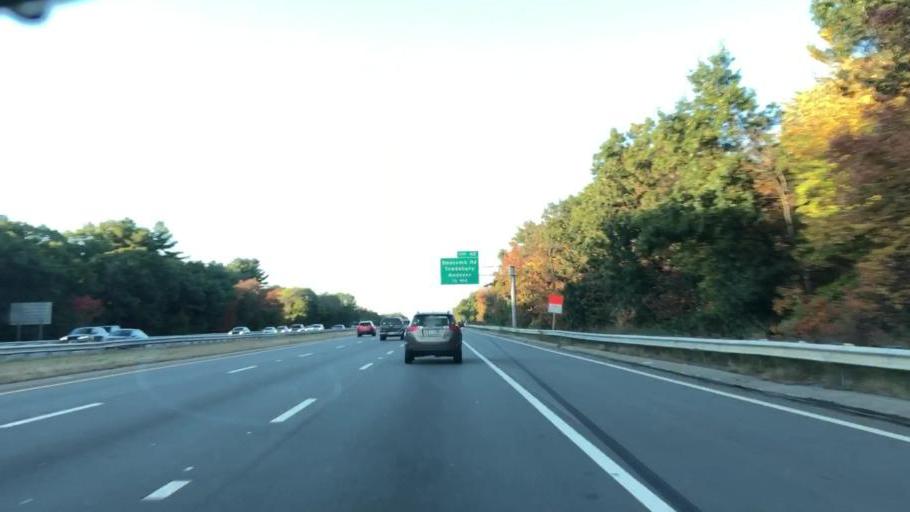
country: US
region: Massachusetts
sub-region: Essex County
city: Andover
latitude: 42.6152
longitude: -71.1748
